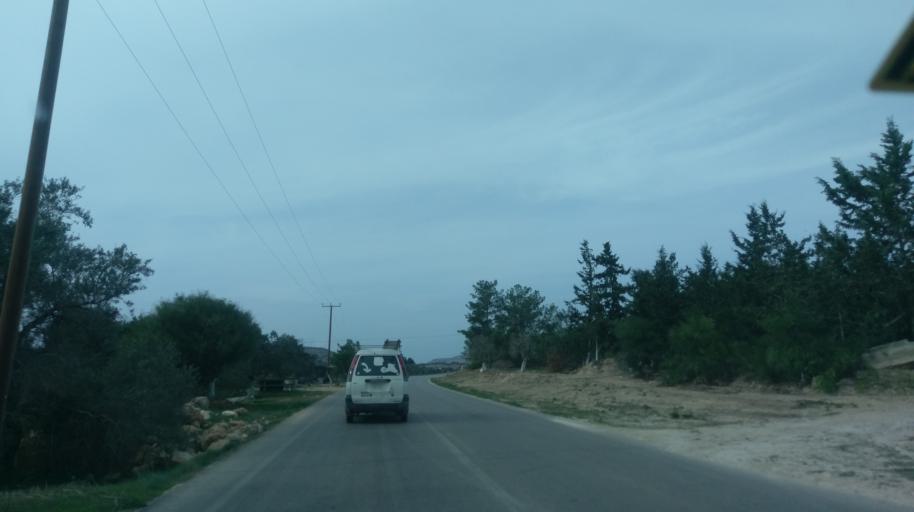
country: CY
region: Ammochostos
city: Leonarisso
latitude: 35.4487
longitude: 34.1317
